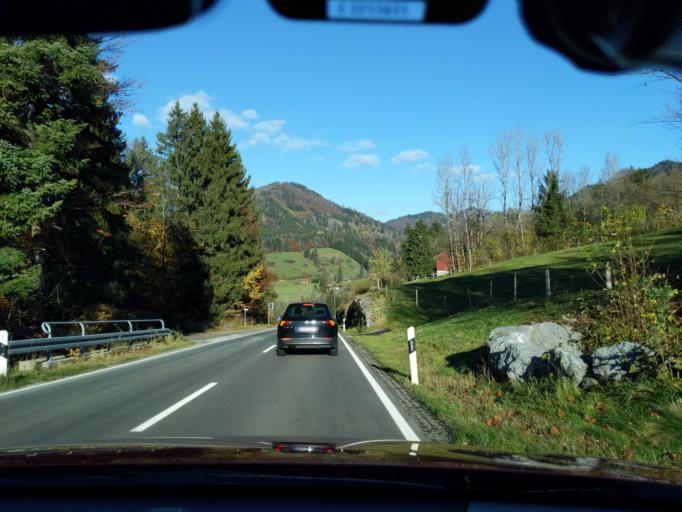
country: DE
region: Bavaria
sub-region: Swabia
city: Oberstaufen
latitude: 47.5372
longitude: 10.0185
